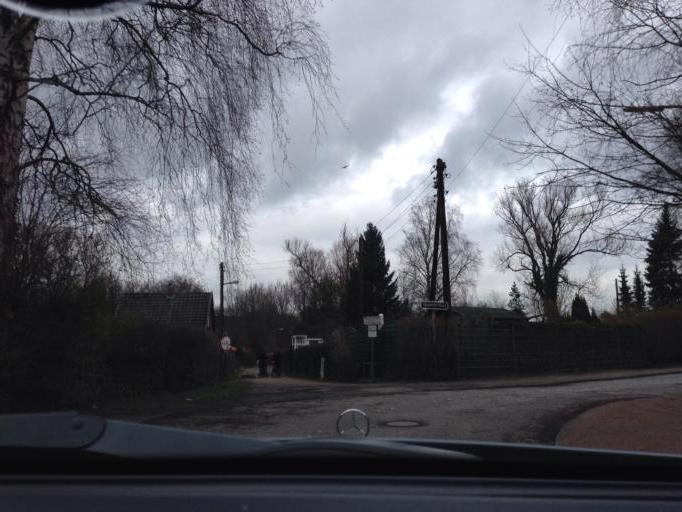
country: DE
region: Hamburg
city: Farmsen-Berne
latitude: 53.5885
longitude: 10.1142
